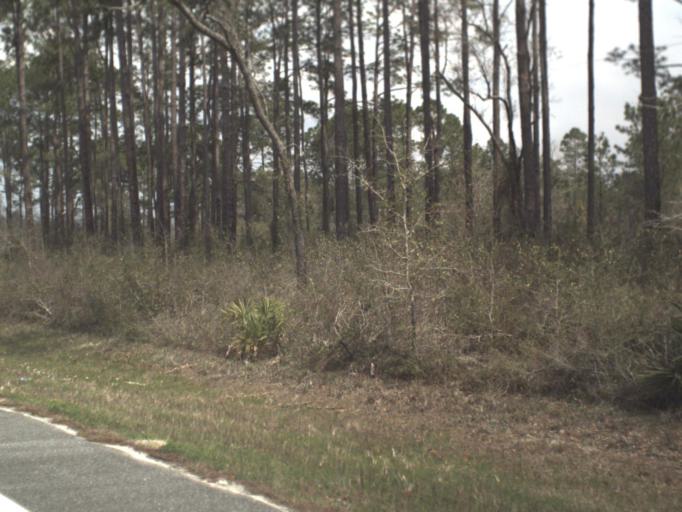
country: US
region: Florida
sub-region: Franklin County
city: Apalachicola
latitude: 29.9166
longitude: -84.9774
